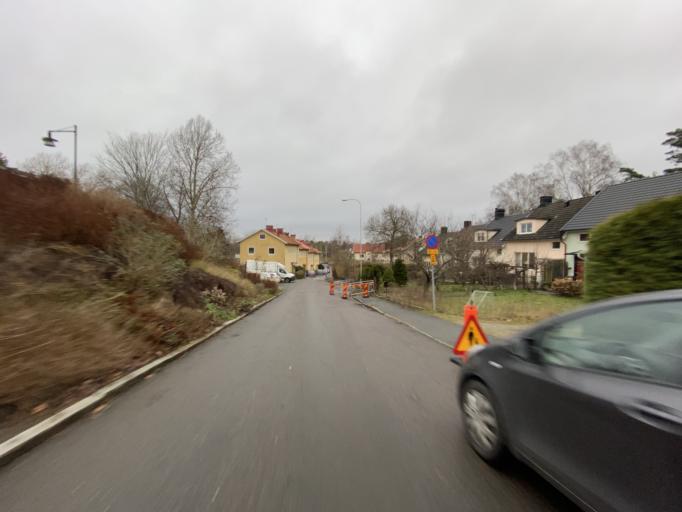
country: SE
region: Vaestra Goetaland
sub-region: Goteborg
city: Eriksbo
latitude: 57.7160
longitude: 12.0398
